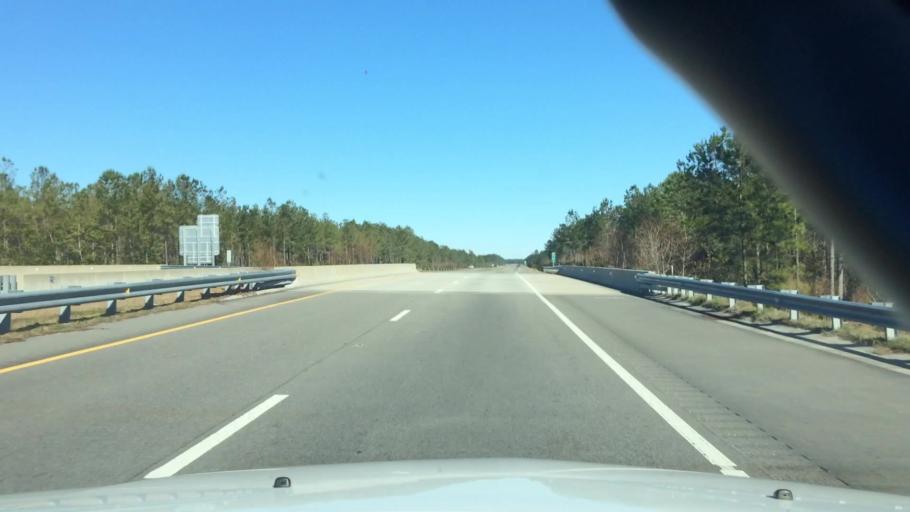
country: US
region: North Carolina
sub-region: Brunswick County
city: Leland
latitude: 34.2182
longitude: -78.0768
